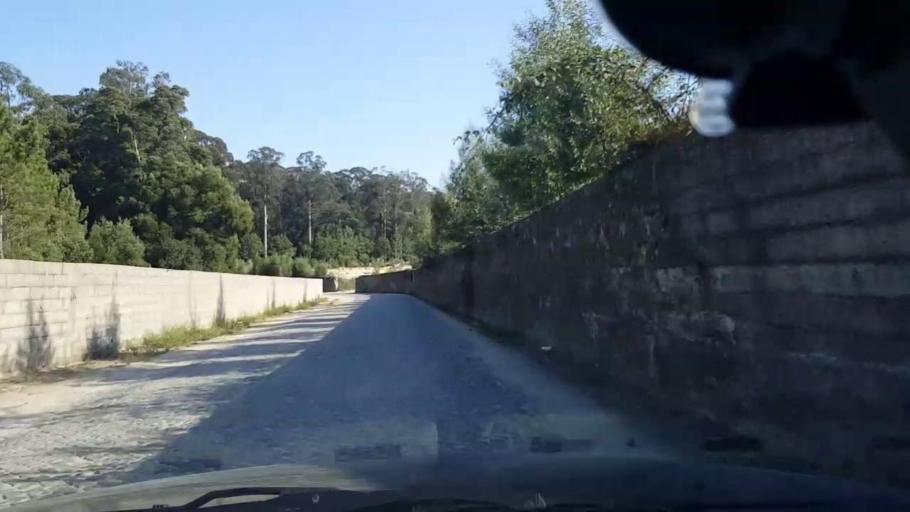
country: PT
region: Porto
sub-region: Vila do Conde
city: Arvore
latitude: 41.3474
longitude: -8.6919
